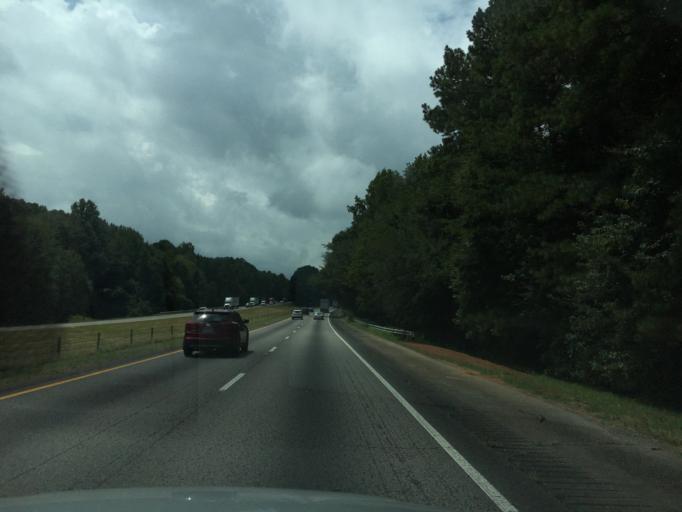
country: US
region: Georgia
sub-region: Jackson County
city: Jefferson
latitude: 34.1402
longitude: -83.6657
